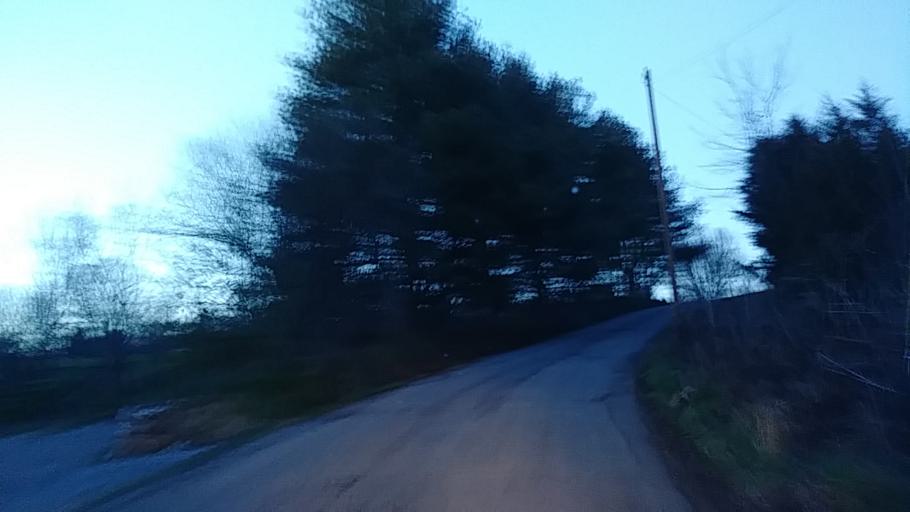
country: US
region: Tennessee
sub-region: Greene County
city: Mosheim
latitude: 36.0650
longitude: -82.9872
